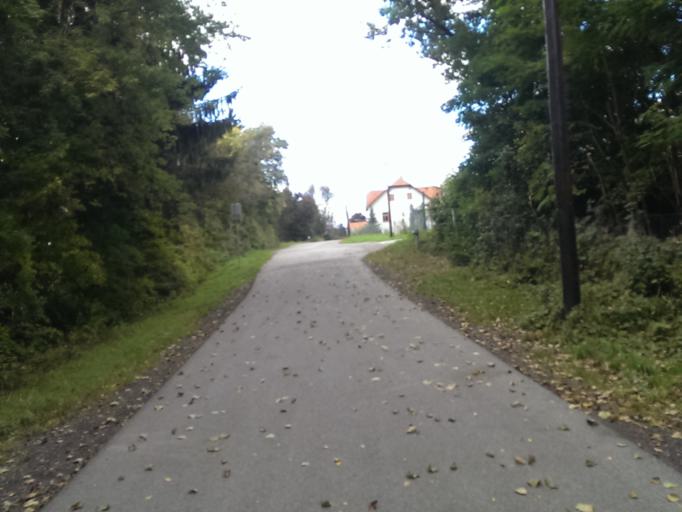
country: AT
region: Styria
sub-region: Politischer Bezirk Graz-Umgebung
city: Raaba
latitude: 47.0372
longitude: 15.4738
